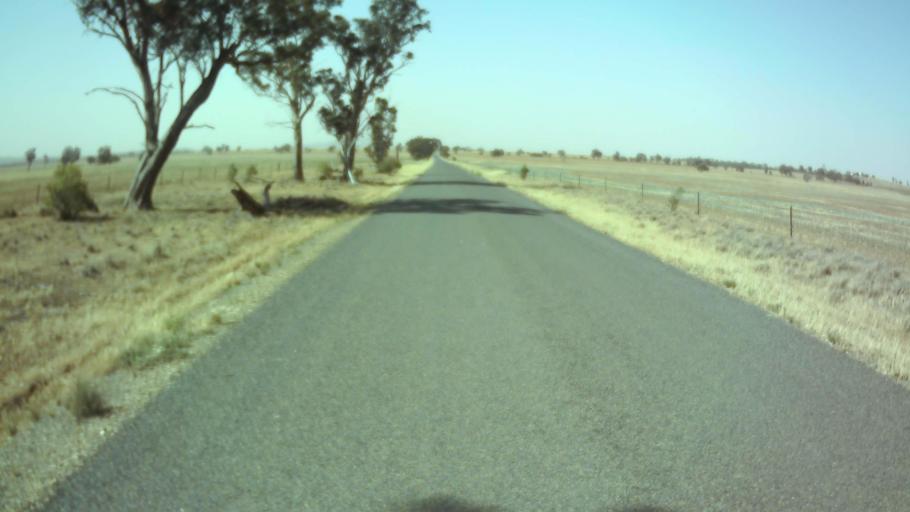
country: AU
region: New South Wales
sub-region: Weddin
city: Grenfell
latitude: -33.8729
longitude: 147.9260
